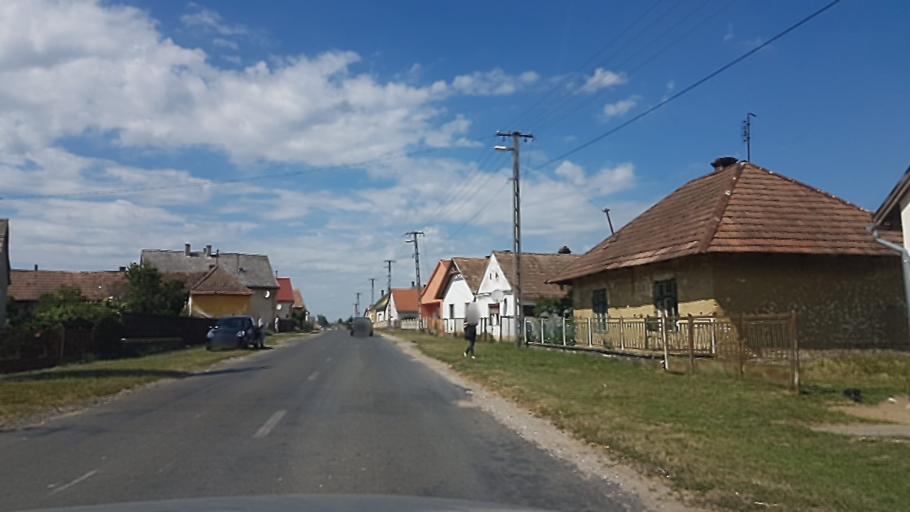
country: HU
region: Somogy
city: Barcs
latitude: 45.9711
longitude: 17.5891
